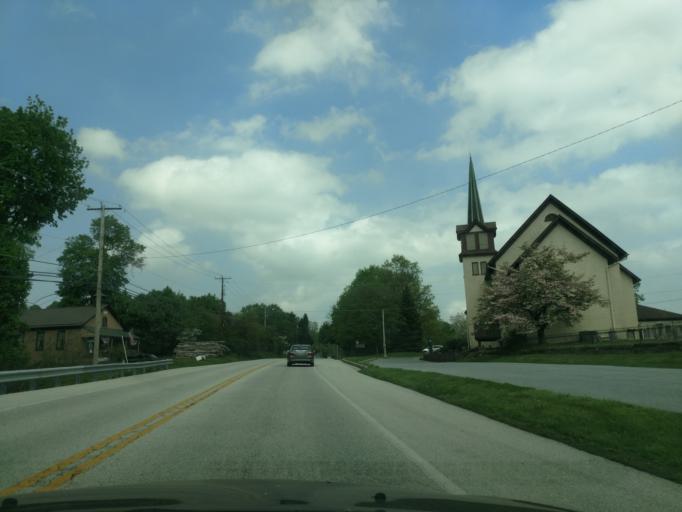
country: US
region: Pennsylvania
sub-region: Montgomery County
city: Stowe
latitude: 40.1739
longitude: -75.7215
